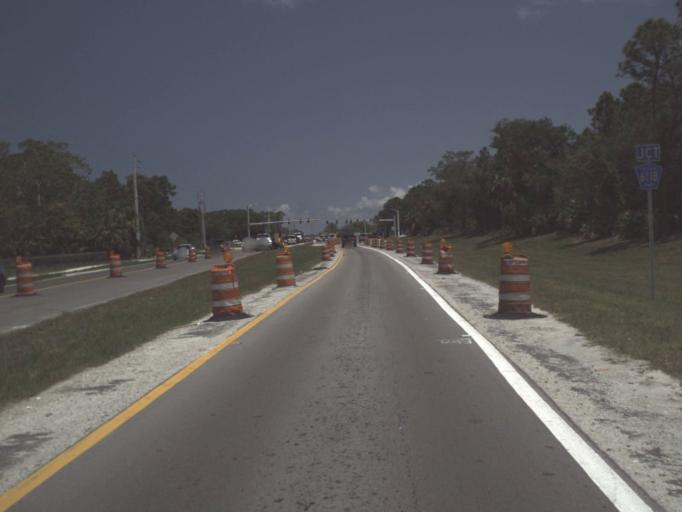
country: US
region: Florida
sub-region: Saint Lucie County
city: White City
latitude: 27.3744
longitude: -80.3699
